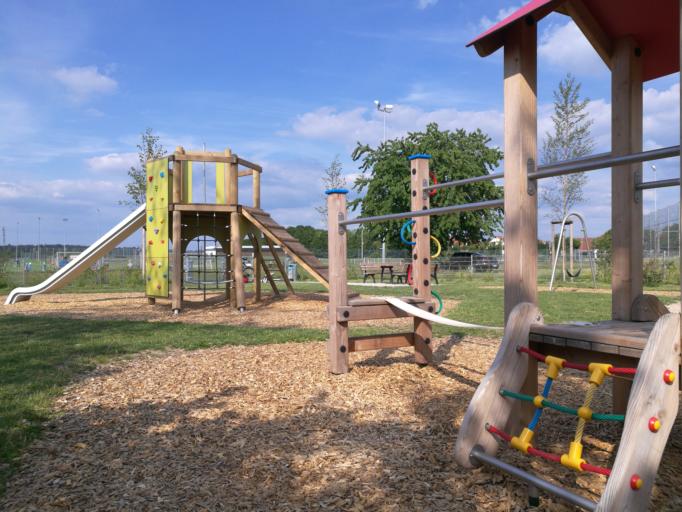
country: DE
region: Bavaria
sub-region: Regierungsbezirk Mittelfranken
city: Seukendorf
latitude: 49.4929
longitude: 10.9066
